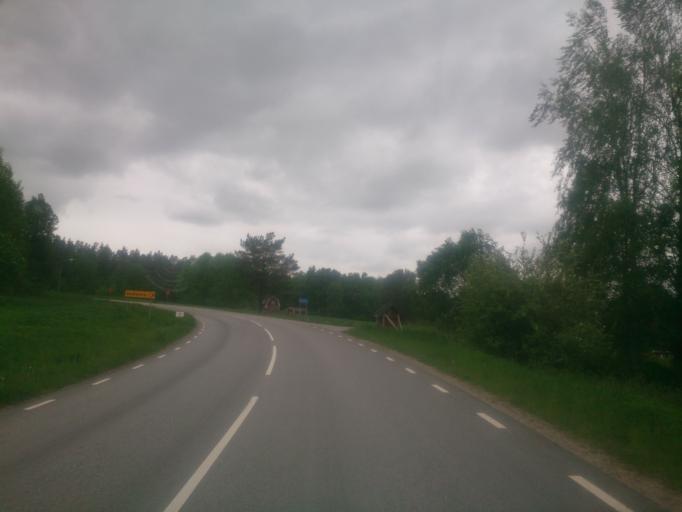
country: SE
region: OEstergoetland
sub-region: Atvidabergs Kommun
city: Atvidaberg
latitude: 58.2210
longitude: 16.0287
